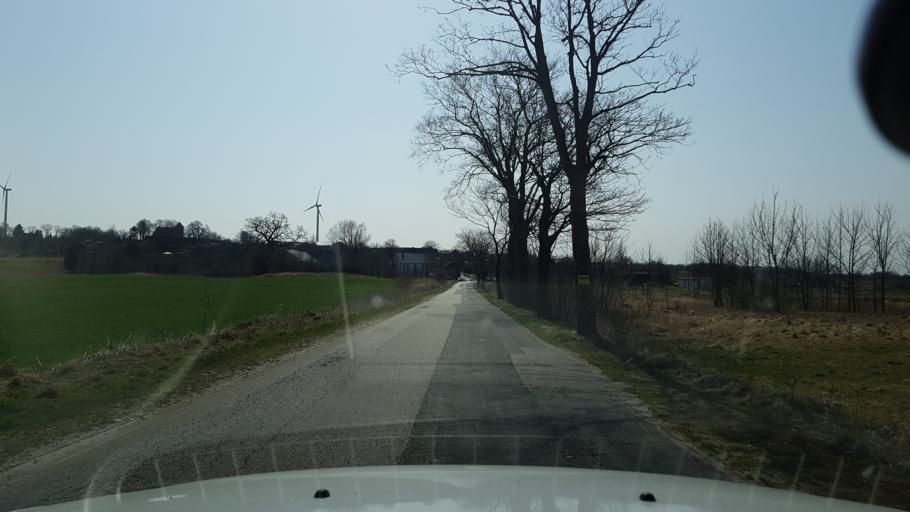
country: PL
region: West Pomeranian Voivodeship
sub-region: Powiat slawienski
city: Darlowo
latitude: 54.4837
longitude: 16.5086
